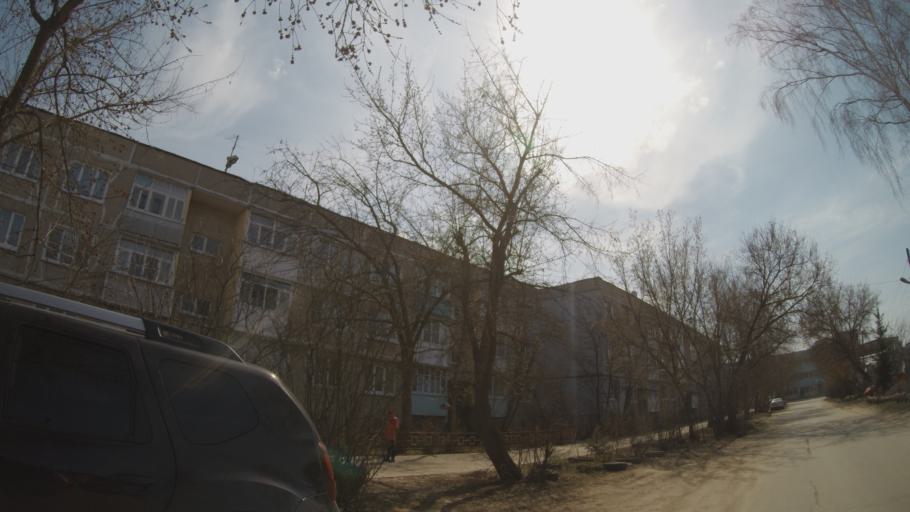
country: RU
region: Nizjnij Novgorod
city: Vyyezdnoye
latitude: 55.3851
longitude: 43.8115
